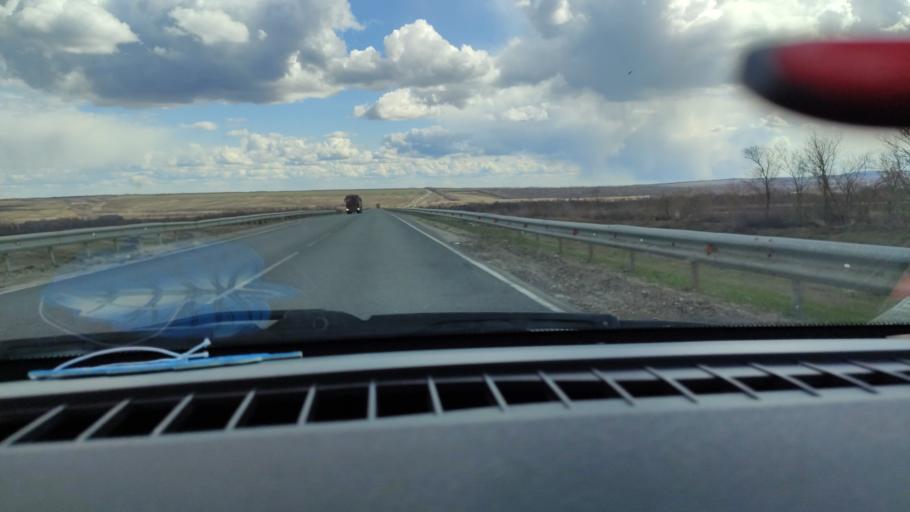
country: RU
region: Saratov
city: Dukhovnitskoye
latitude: 52.7530
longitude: 48.2471
